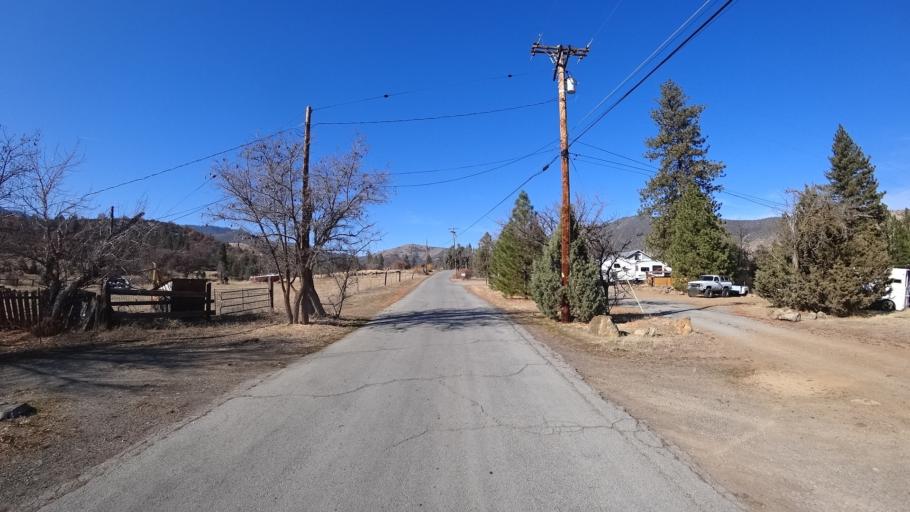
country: US
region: California
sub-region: Siskiyou County
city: Yreka
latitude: 41.7634
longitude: -122.6260
